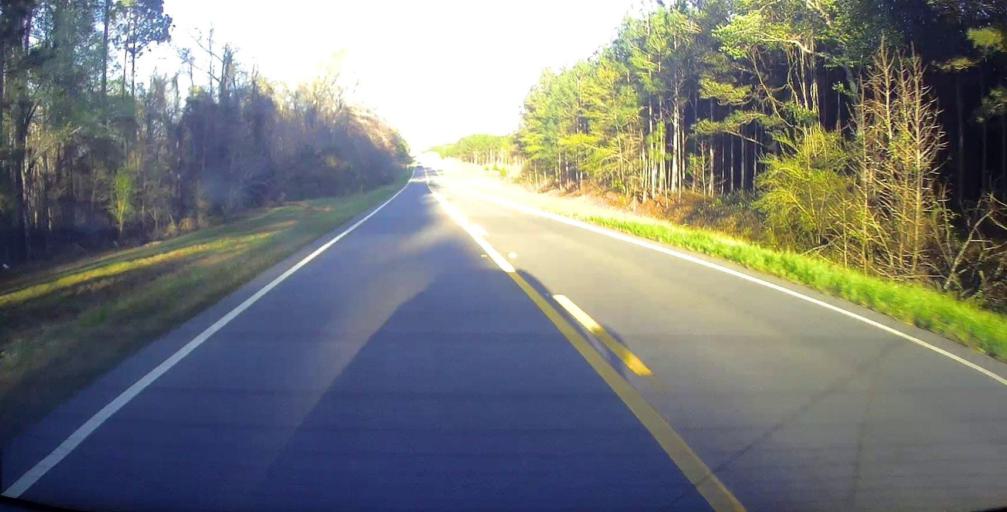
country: US
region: Georgia
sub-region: Wilcox County
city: Abbeville
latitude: 31.9862
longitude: -83.3392
